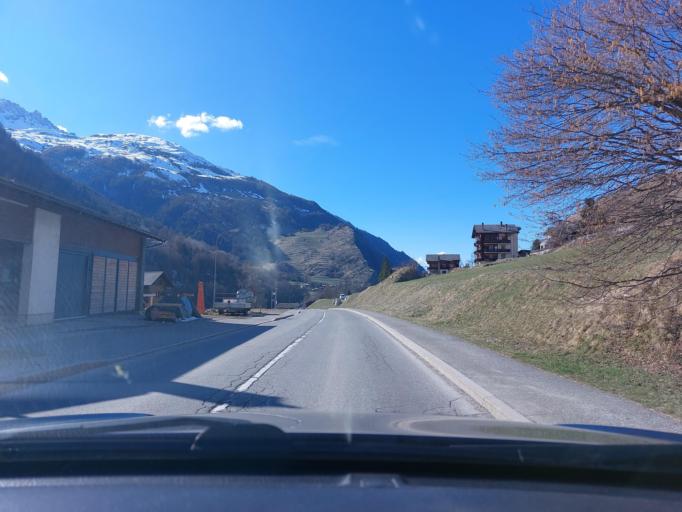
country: CH
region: Valais
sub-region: Herens District
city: Evolene
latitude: 46.1153
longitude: 7.4925
